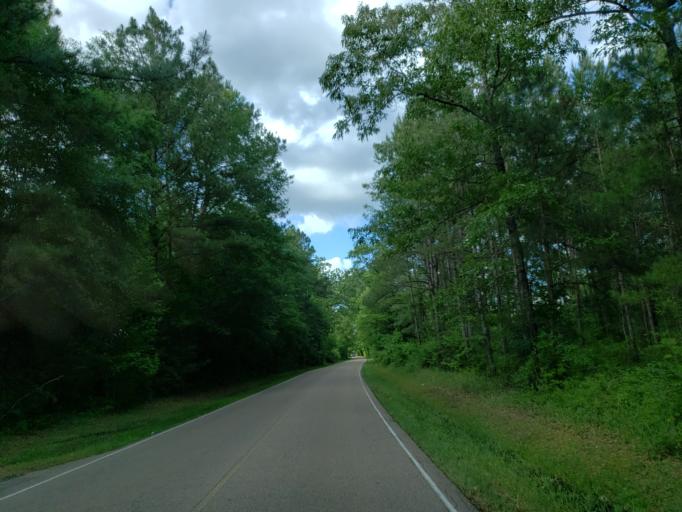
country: US
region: Mississippi
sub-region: Forrest County
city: Hattiesburg
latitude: 31.2501
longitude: -89.2410
